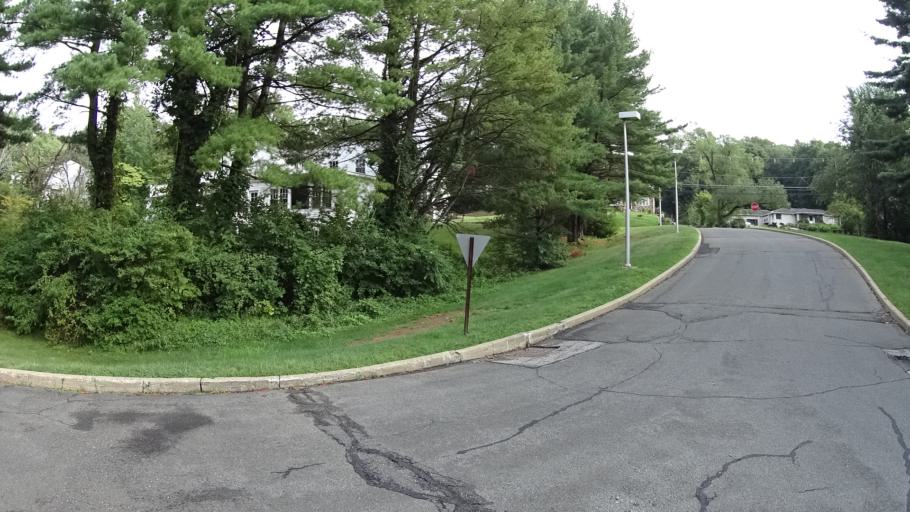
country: US
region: New Jersey
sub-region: Union County
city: Berkeley Heights
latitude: 40.7049
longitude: -74.4346
